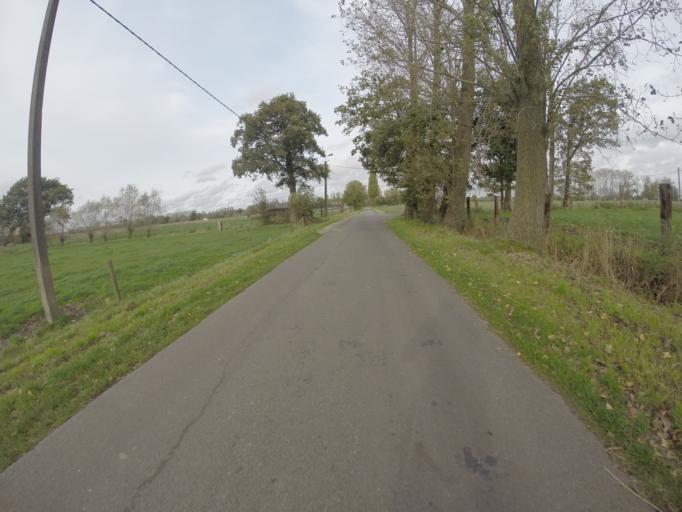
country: BE
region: Flanders
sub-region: Provincie Oost-Vlaanderen
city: Maldegem
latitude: 51.1799
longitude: 3.4282
